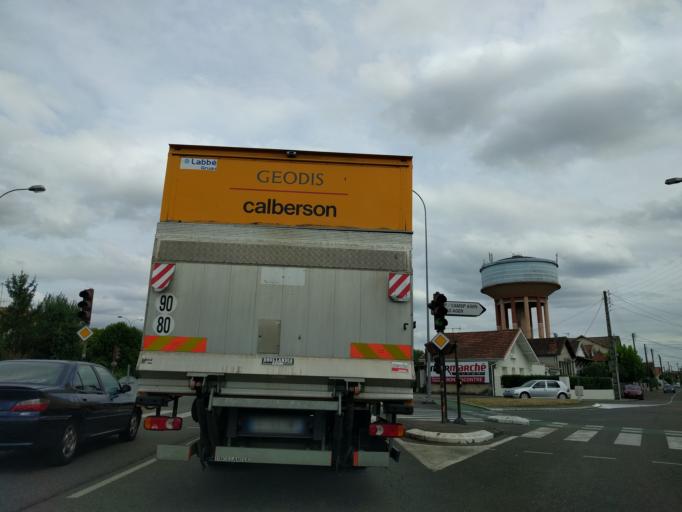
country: FR
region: Aquitaine
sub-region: Departement du Lot-et-Garonne
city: Agen
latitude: 44.1940
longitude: 0.6296
